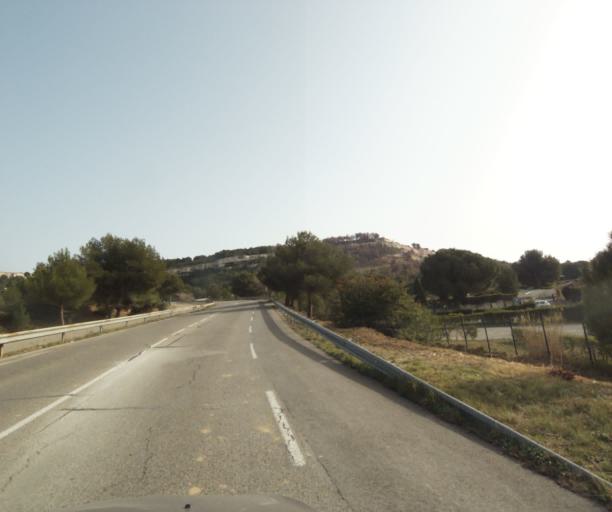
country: FR
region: Provence-Alpes-Cote d'Azur
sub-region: Departement des Bouches-du-Rhone
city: Vitrolles
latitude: 43.4684
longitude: 5.2348
